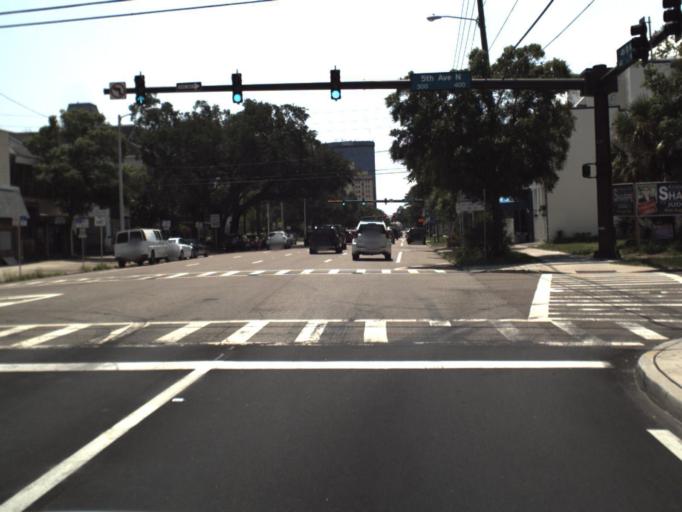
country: US
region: Florida
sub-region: Pinellas County
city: Saint Petersburg
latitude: 27.7778
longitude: -82.6386
